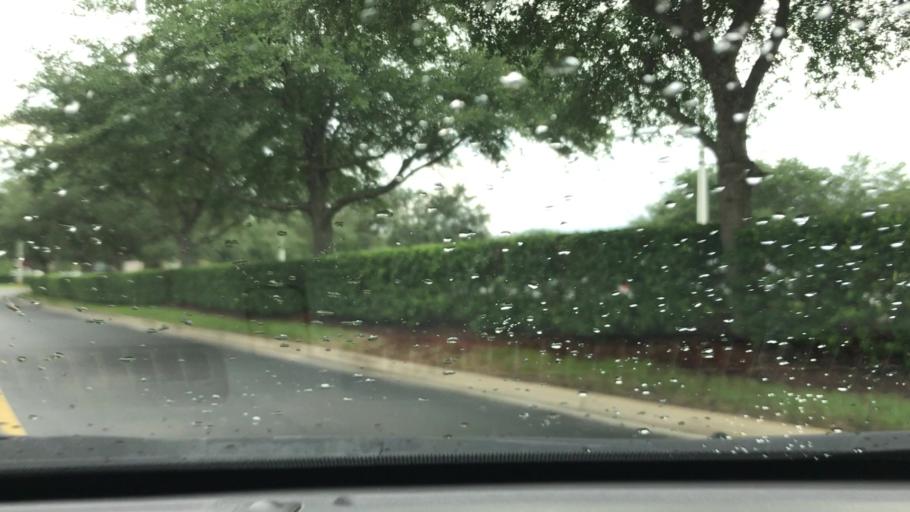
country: US
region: Florida
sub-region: Orange County
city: Williamsburg
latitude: 28.3875
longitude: -81.4860
